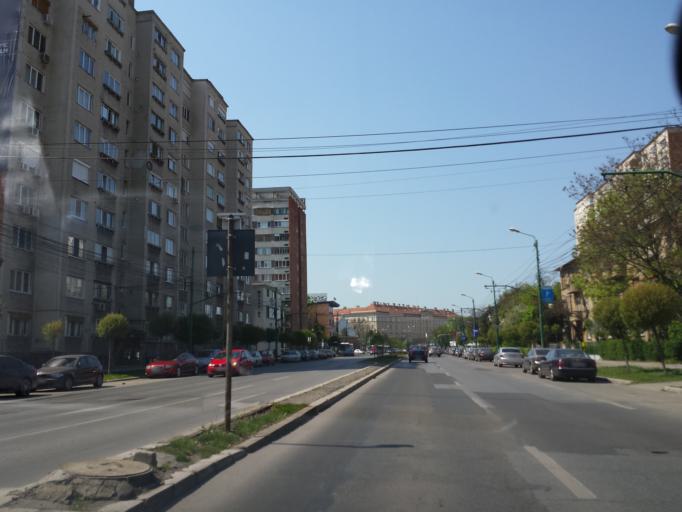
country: RO
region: Timis
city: Timisoara
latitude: 45.7589
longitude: 21.2362
